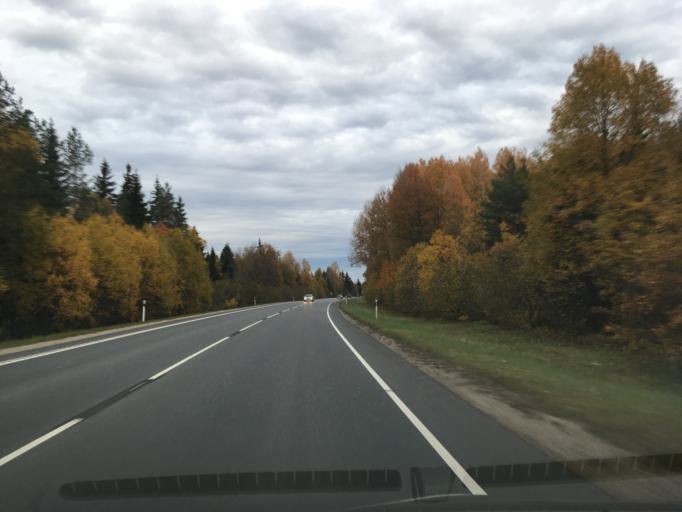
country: EE
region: Harju
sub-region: Nissi vald
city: Turba
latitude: 59.1093
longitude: 24.2561
